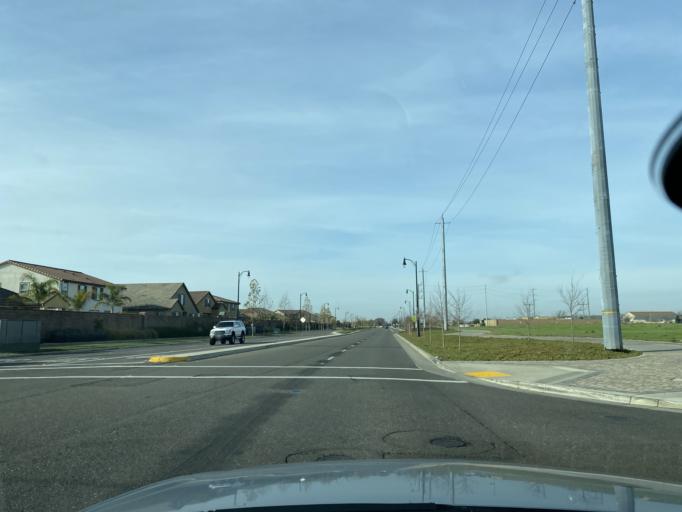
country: US
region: California
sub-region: Sacramento County
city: Elk Grove
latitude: 38.3945
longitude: -121.3923
